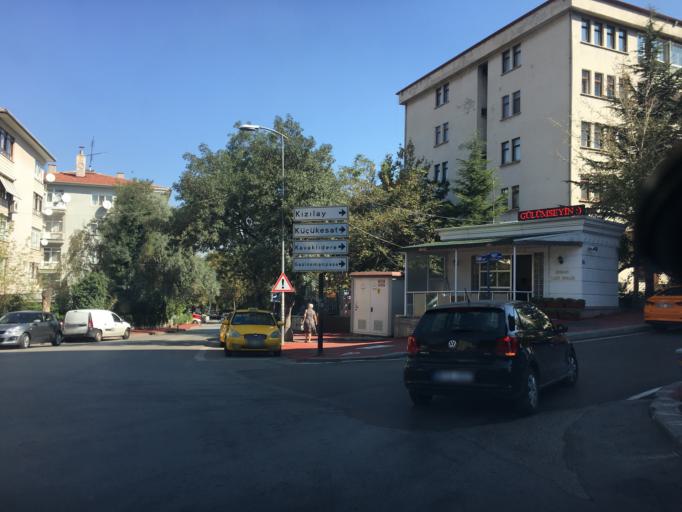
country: TR
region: Ankara
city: Ankara
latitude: 39.8997
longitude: 32.8505
